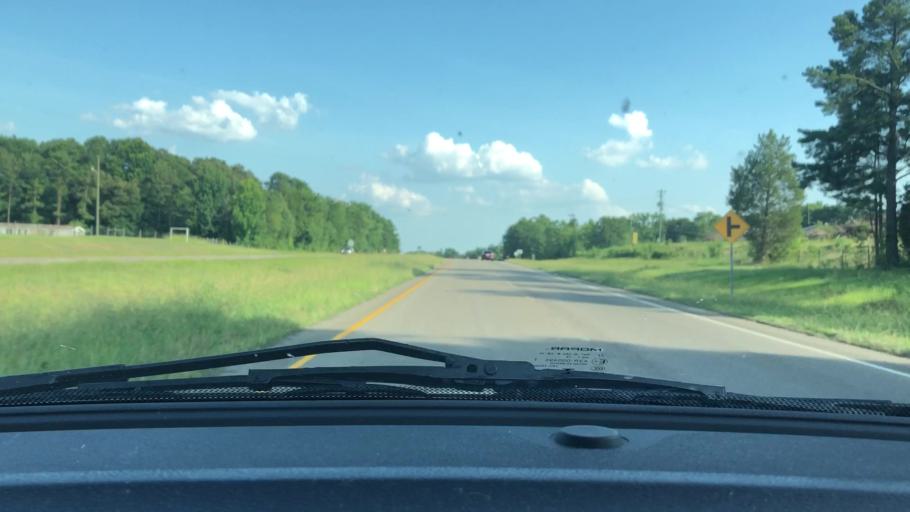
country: US
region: North Carolina
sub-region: Chatham County
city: Farmville
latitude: 35.5805
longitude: -79.3115
